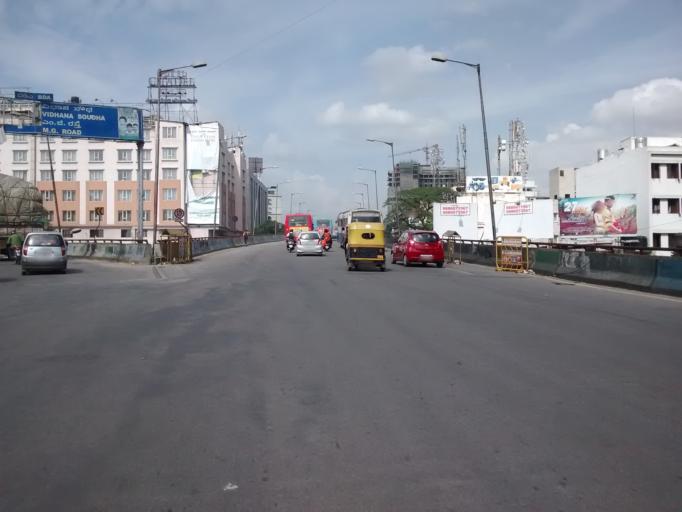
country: IN
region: Karnataka
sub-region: Bangalore Urban
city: Bangalore
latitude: 12.9807
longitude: 77.5744
